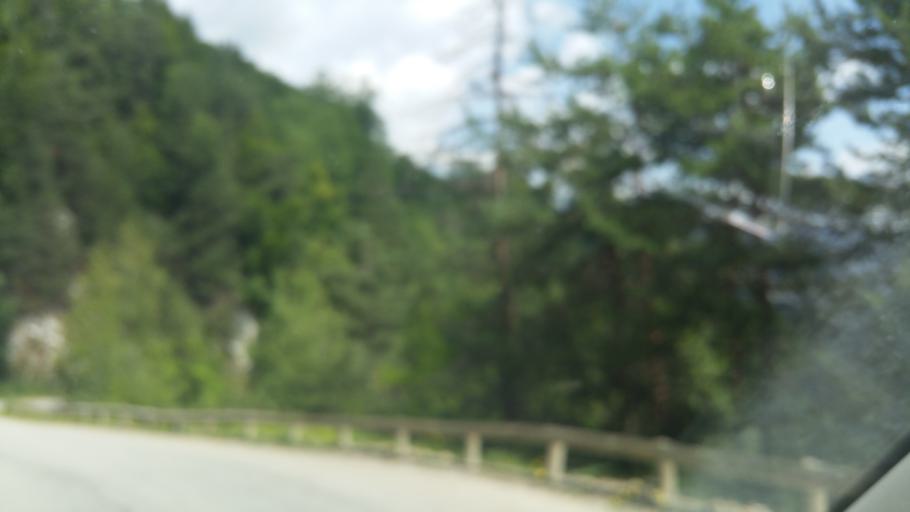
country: FR
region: Rhone-Alpes
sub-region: Departement de la Savoie
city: Saint-Jean-de-Maurienne
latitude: 45.2291
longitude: 6.3104
